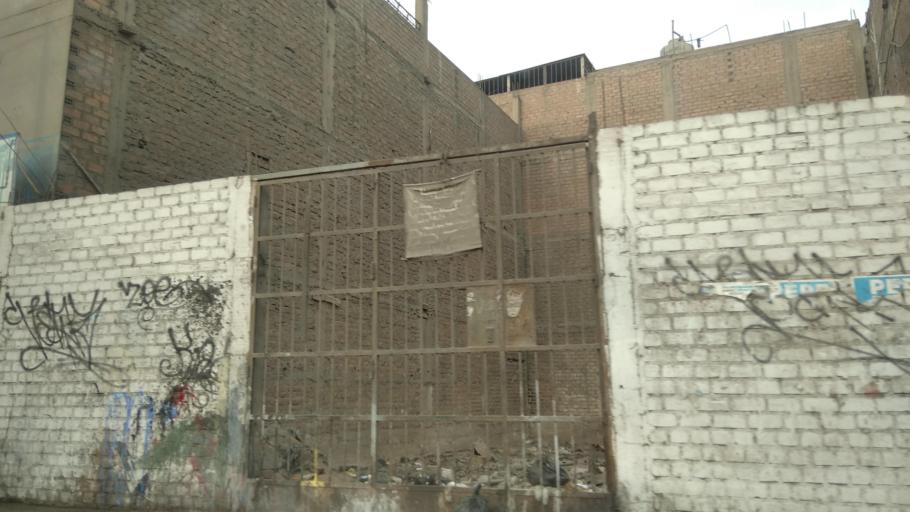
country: PE
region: Lima
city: Lima
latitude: -12.0130
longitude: -76.9976
